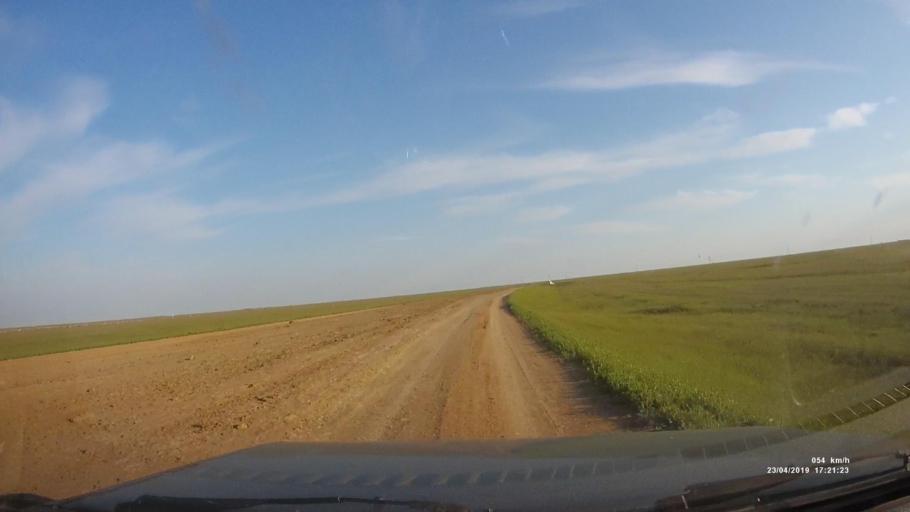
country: RU
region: Kalmykiya
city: Priyutnoye
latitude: 46.1766
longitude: 43.5051
